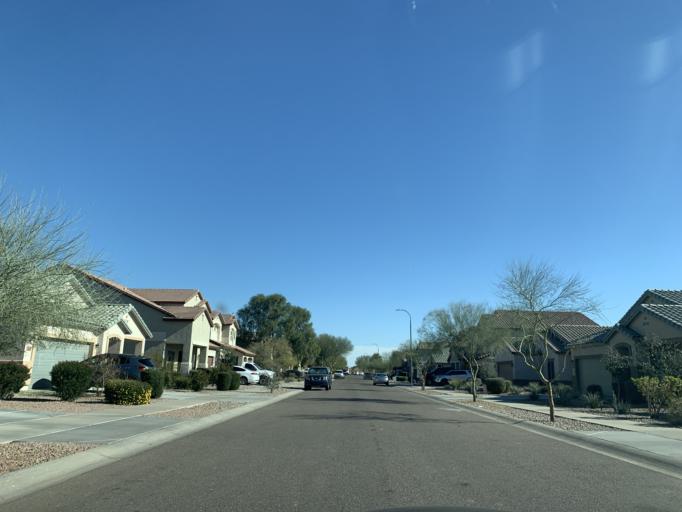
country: US
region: Arizona
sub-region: Maricopa County
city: Laveen
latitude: 33.3974
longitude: -112.1321
